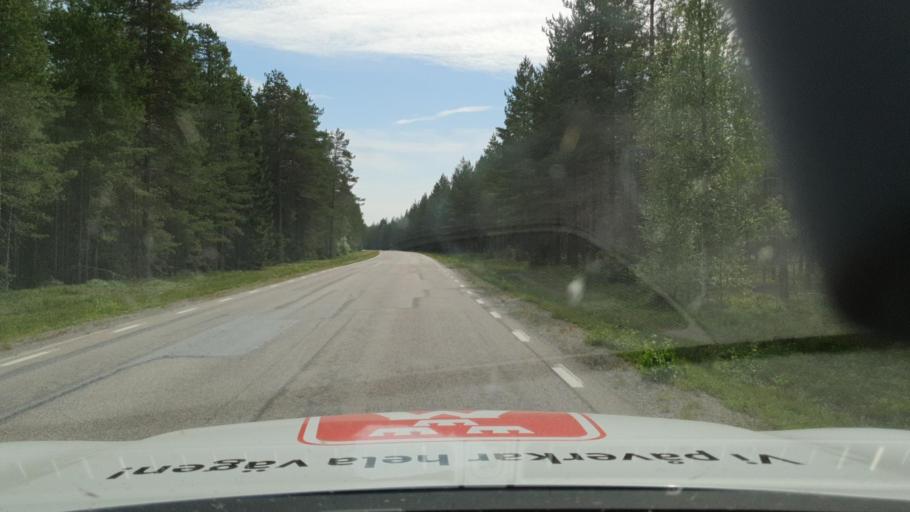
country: SE
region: Vaesterbotten
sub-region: Umea Kommun
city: Roback
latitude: 63.8671
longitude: 20.1458
